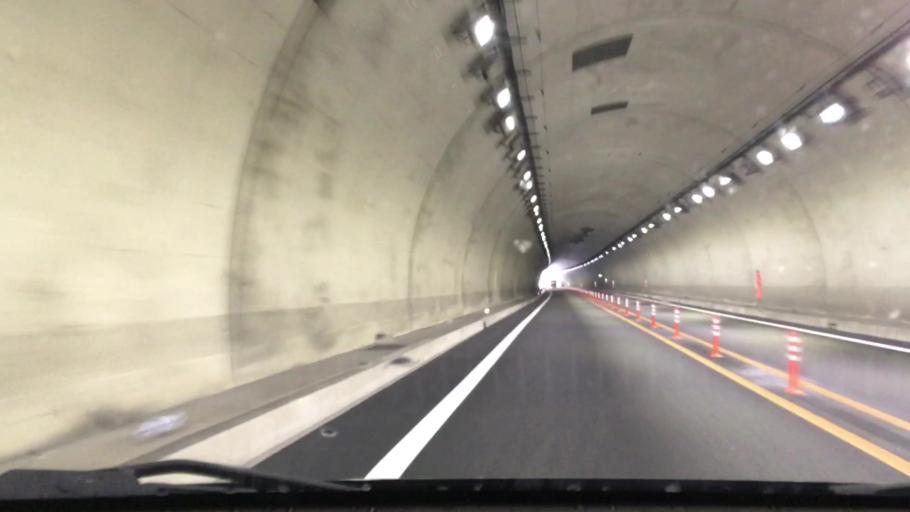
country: JP
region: Kagoshima
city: Kokubu-matsuki
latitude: 31.7310
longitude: 130.8380
